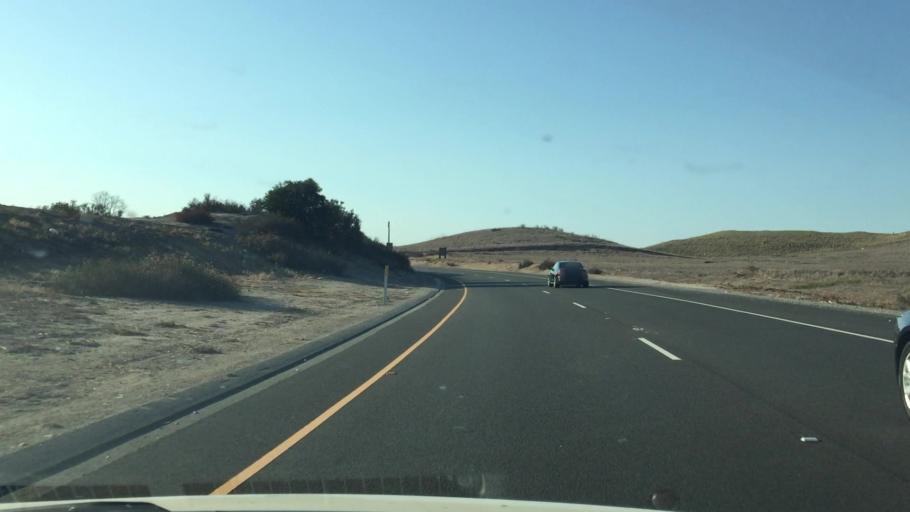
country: US
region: California
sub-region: Orange County
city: Laguna Woods
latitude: 33.6233
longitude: -117.7559
